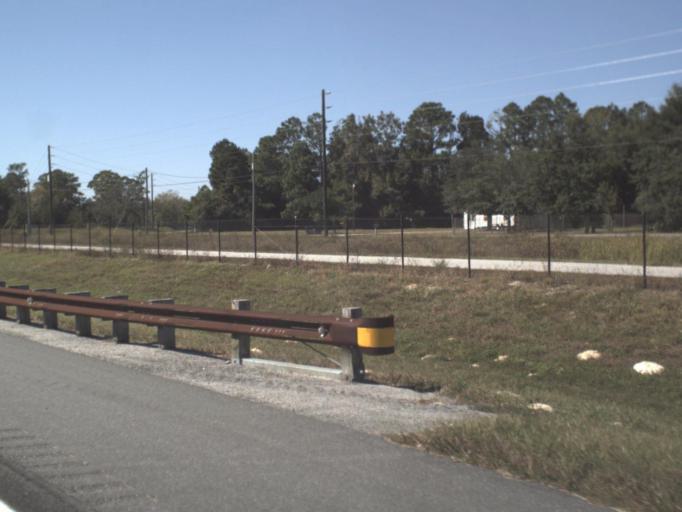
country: US
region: Florida
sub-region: Pasco County
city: Shady Hills
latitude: 28.4123
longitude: -82.5026
